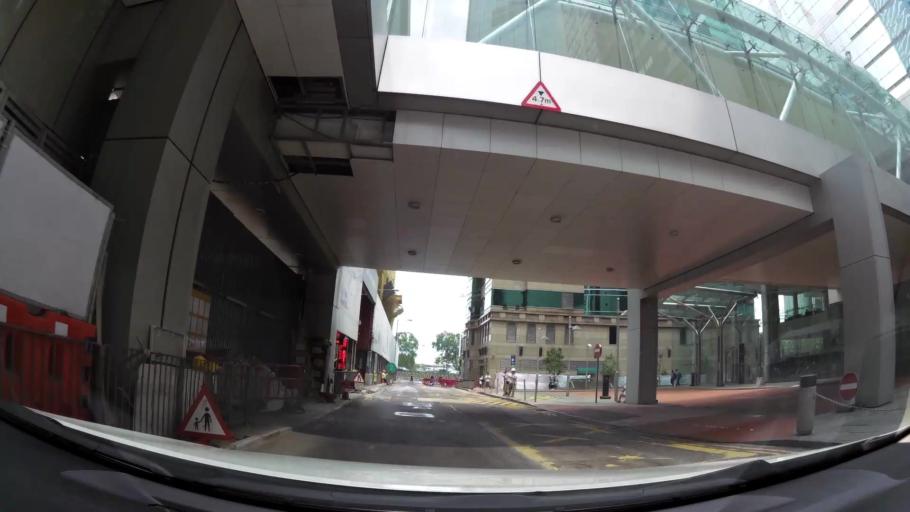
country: HK
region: Wanchai
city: Wan Chai
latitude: 22.2869
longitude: 114.2129
